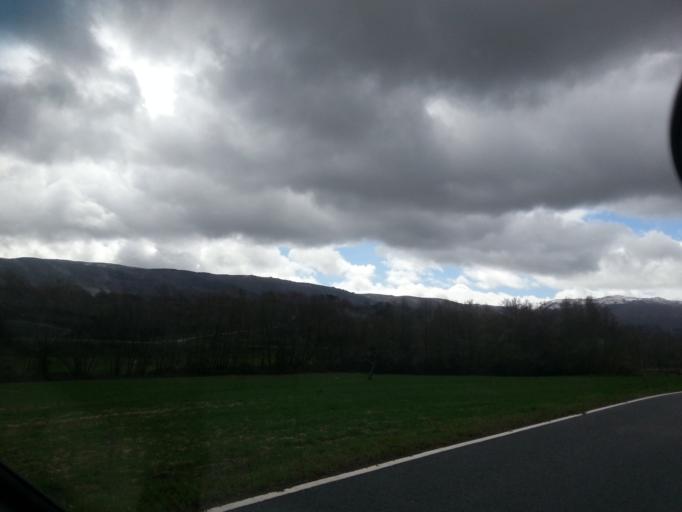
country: PT
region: Guarda
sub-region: Fornos de Algodres
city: Fornos de Algodres
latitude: 40.5711
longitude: -7.4691
